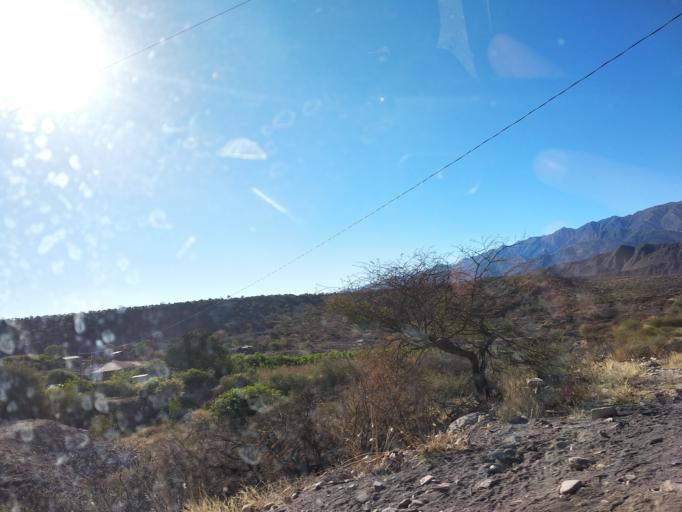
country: BO
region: Cochabamba
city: Mizque
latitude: -18.0779
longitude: -65.7451
